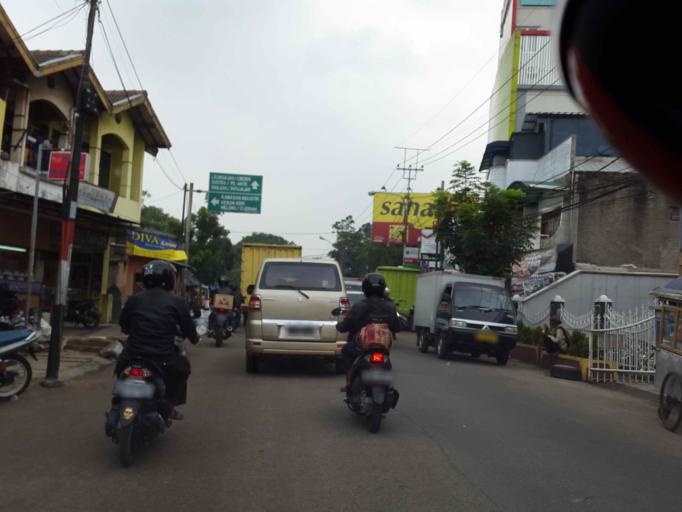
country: ID
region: West Java
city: Cimahi
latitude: -6.9003
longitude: 107.5476
